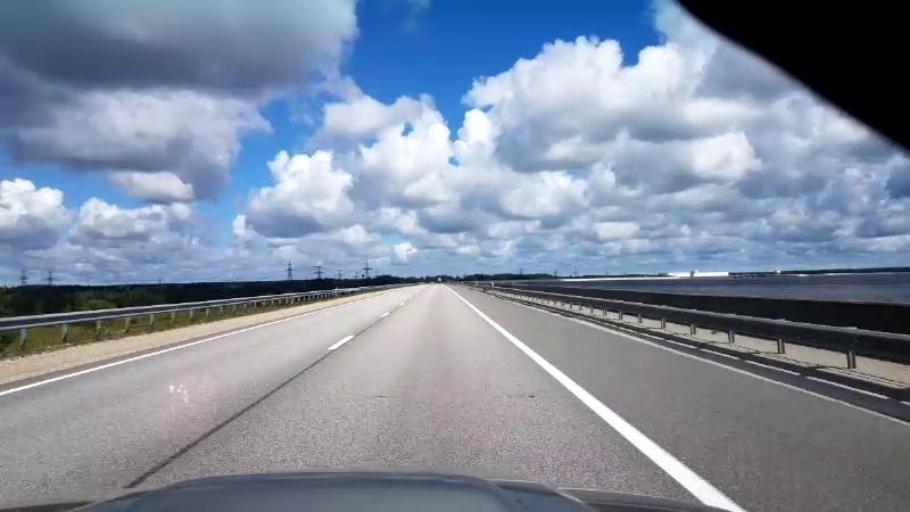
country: LV
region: Kekava
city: Kekava
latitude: 56.8359
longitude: 24.2690
